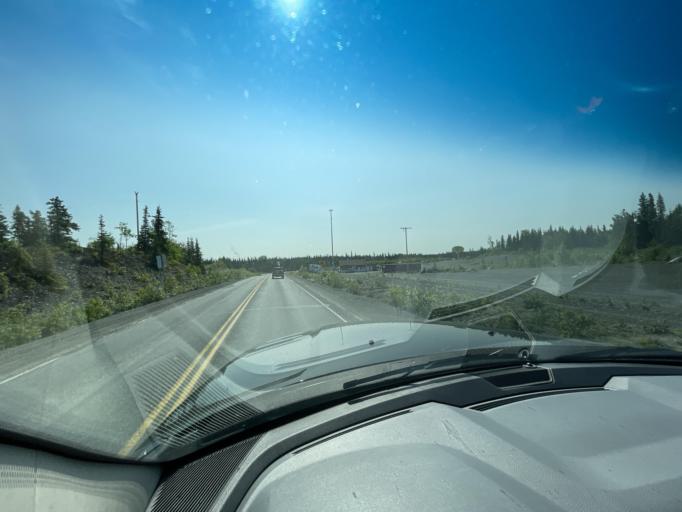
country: US
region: Alaska
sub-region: Kenai Peninsula Borough
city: Cohoe
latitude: 60.2982
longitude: -151.2788
